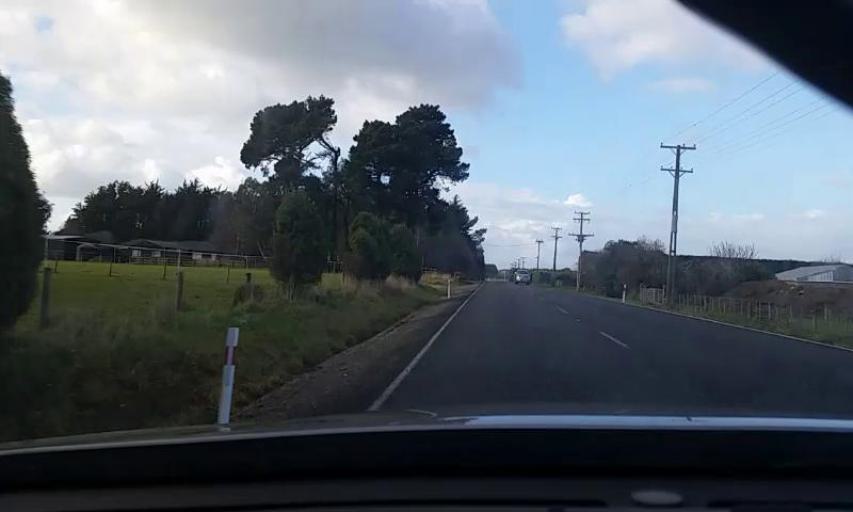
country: NZ
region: Southland
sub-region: Invercargill City
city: Invercargill
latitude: -46.3815
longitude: 168.4429
